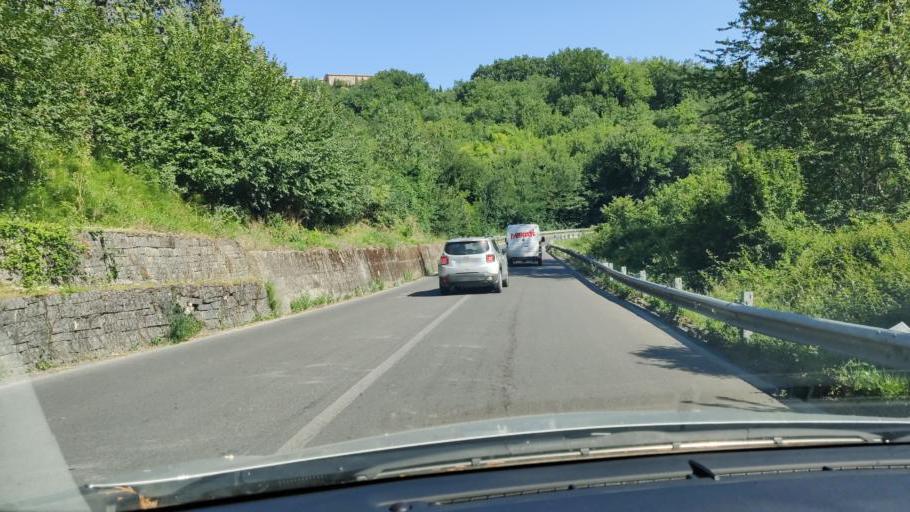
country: IT
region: Umbria
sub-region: Provincia di Perugia
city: Todi
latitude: 42.7836
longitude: 12.4150
